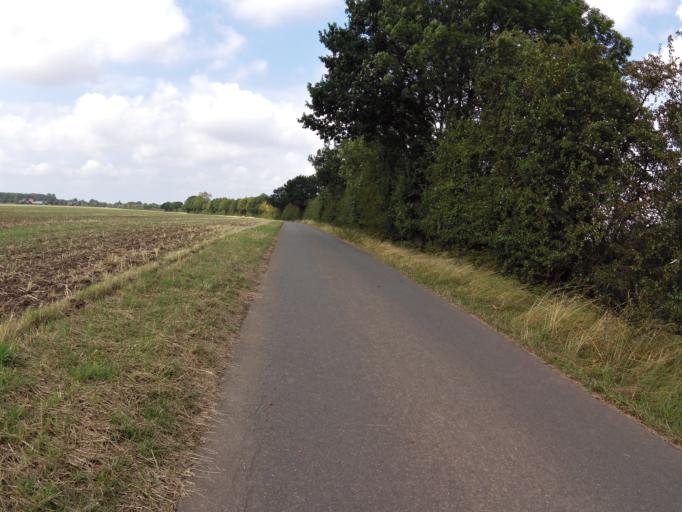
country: DE
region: Lower Saxony
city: Bucken
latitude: 52.7751
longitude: 9.1633
